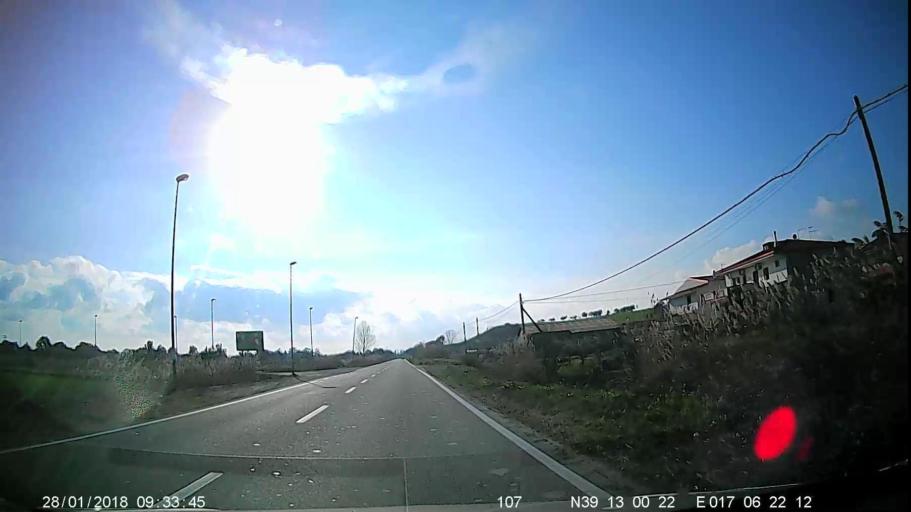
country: IT
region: Calabria
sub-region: Provincia di Crotone
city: Tronca
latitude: 39.2163
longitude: 17.1064
